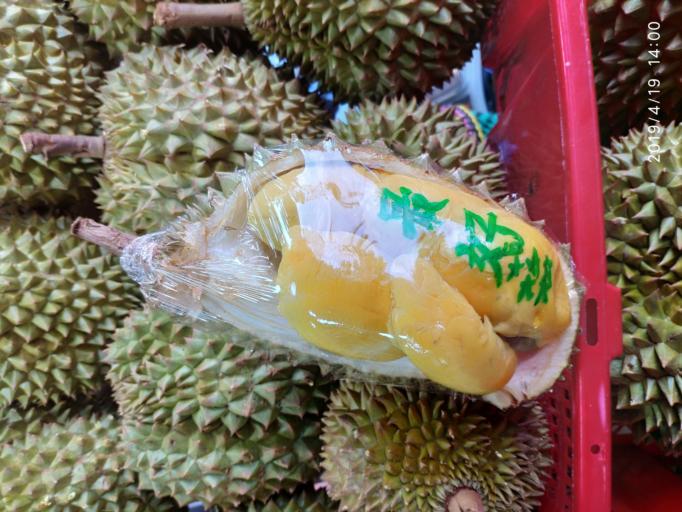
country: MY
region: Johor
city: Johor Bahru
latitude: 1.4860
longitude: 103.7617
